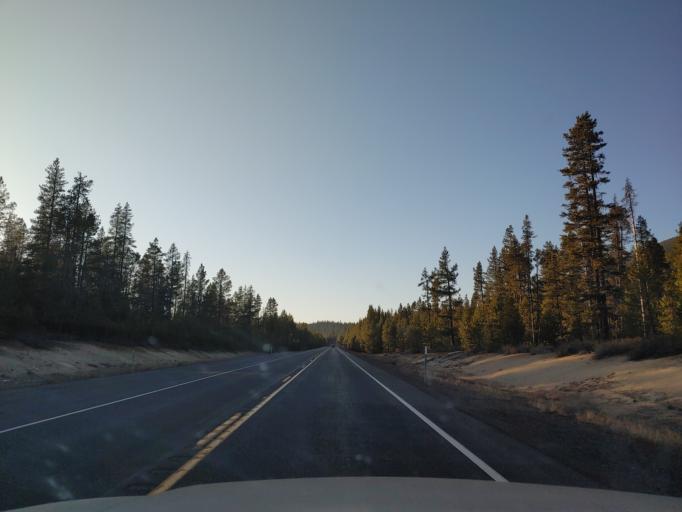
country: US
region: Oregon
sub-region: Deschutes County
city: La Pine
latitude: 43.4350
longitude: -121.8586
